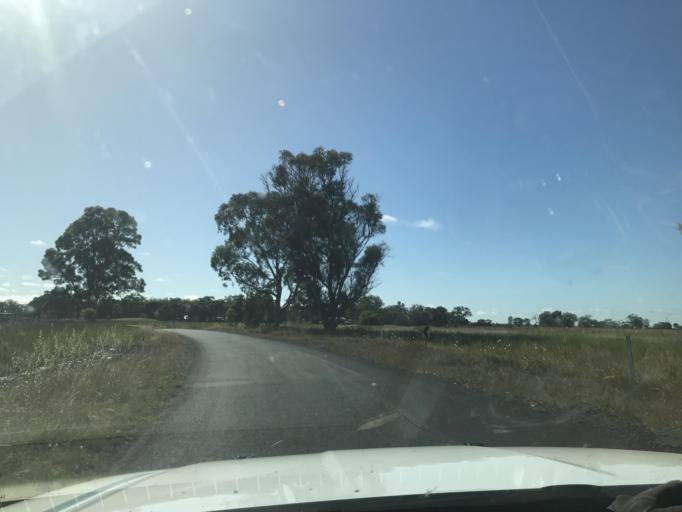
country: AU
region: Victoria
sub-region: Horsham
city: Horsham
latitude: -37.0304
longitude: 141.7200
